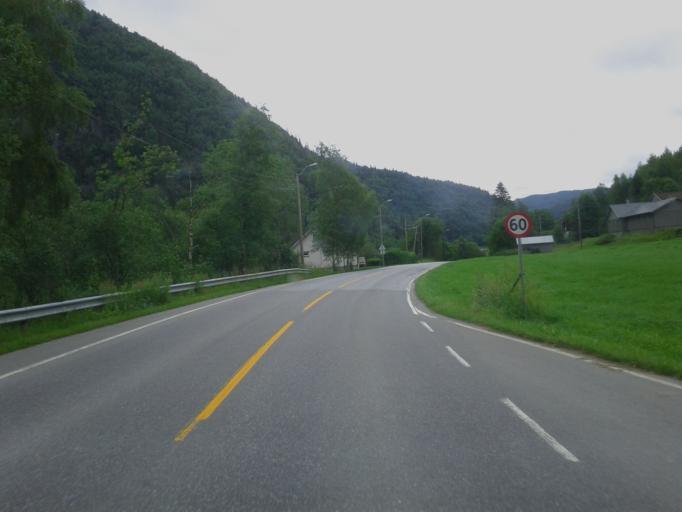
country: NO
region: Sor-Trondelag
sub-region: Midtre Gauldal
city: Storen
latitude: 63.0144
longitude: 10.4391
